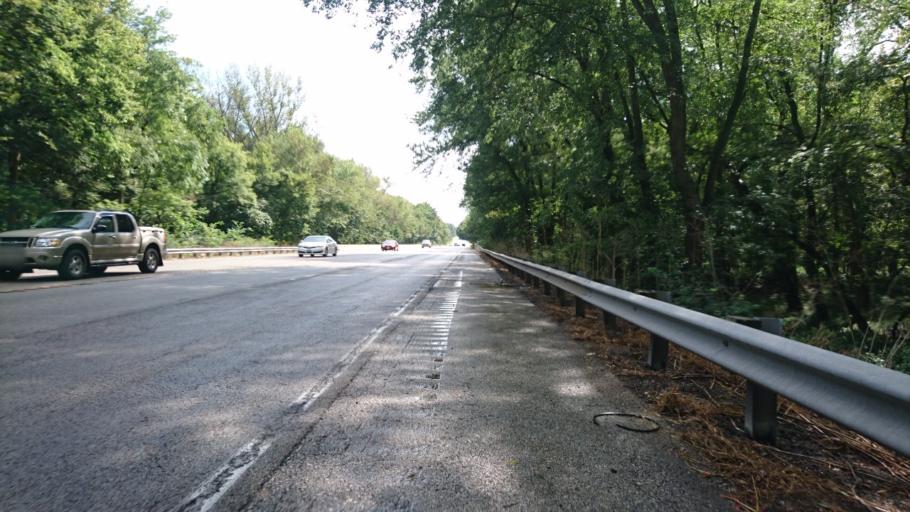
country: US
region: Illinois
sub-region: Sangamon County
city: Sherman
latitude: 39.8688
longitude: -89.6141
